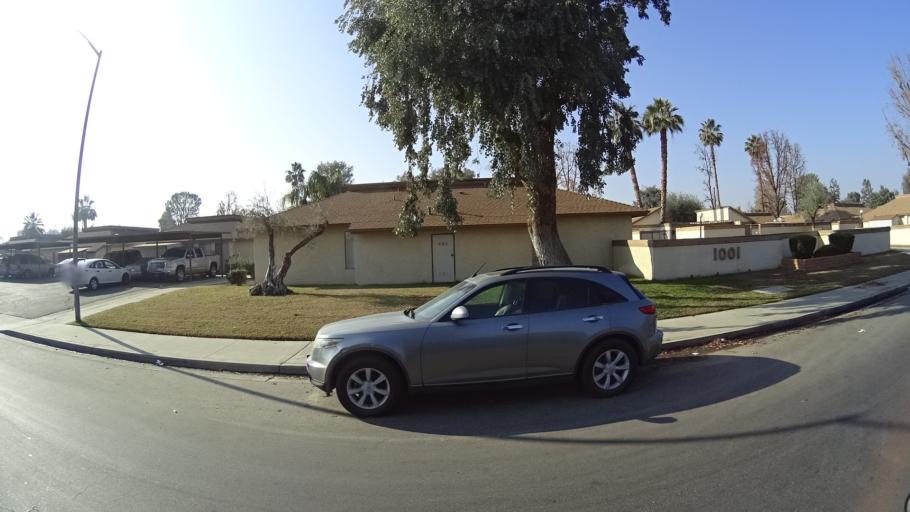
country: US
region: California
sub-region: Kern County
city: Bakersfield
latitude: 35.3455
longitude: -119.0530
